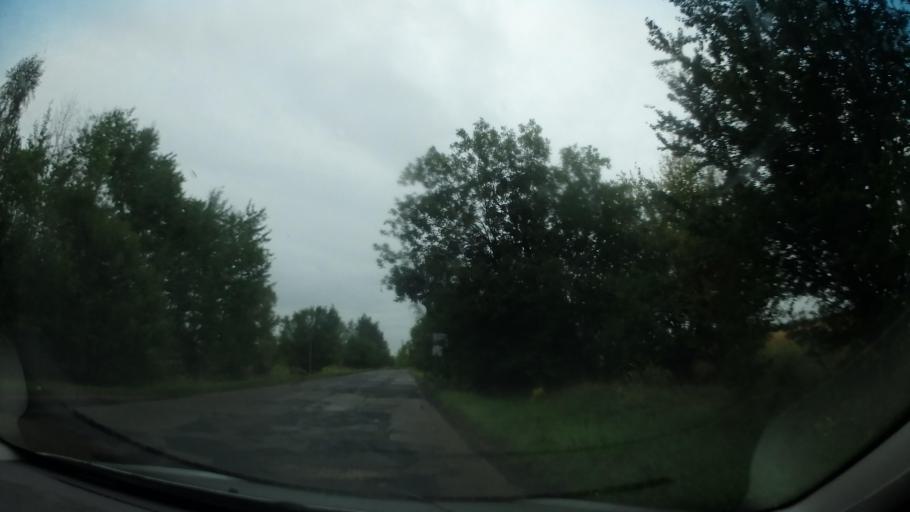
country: CZ
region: Central Bohemia
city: Milovice
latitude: 50.2414
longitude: 14.8971
